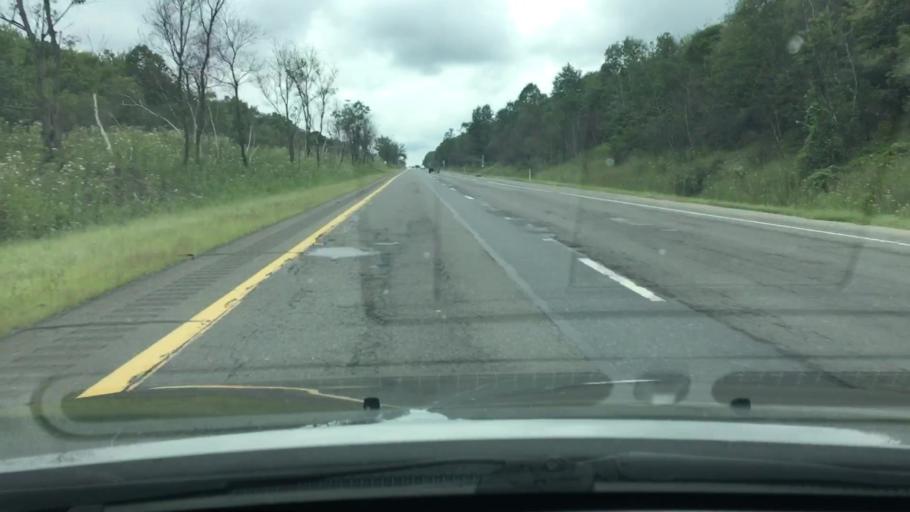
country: US
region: Pennsylvania
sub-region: Schuylkill County
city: Frackville
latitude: 40.7727
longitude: -76.2325
